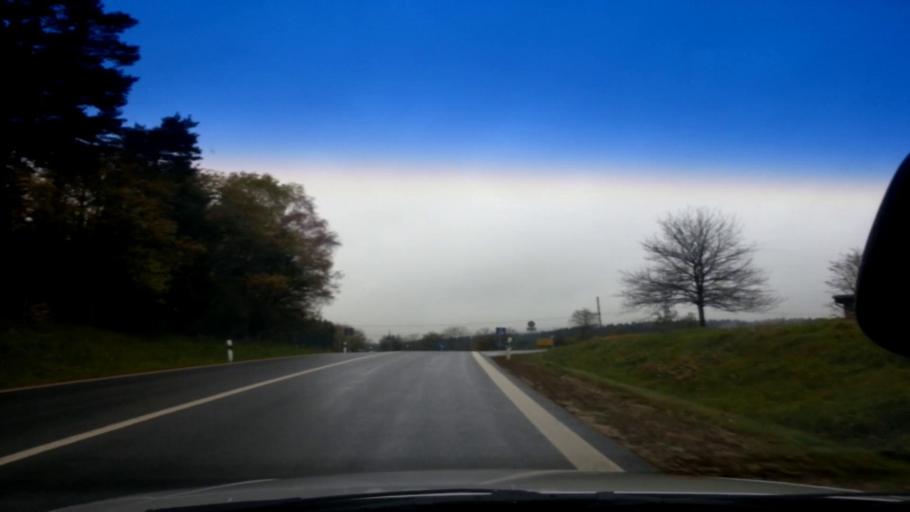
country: DE
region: Bavaria
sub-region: Upper Franconia
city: Wattendorf
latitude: 49.9880
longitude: 11.1210
